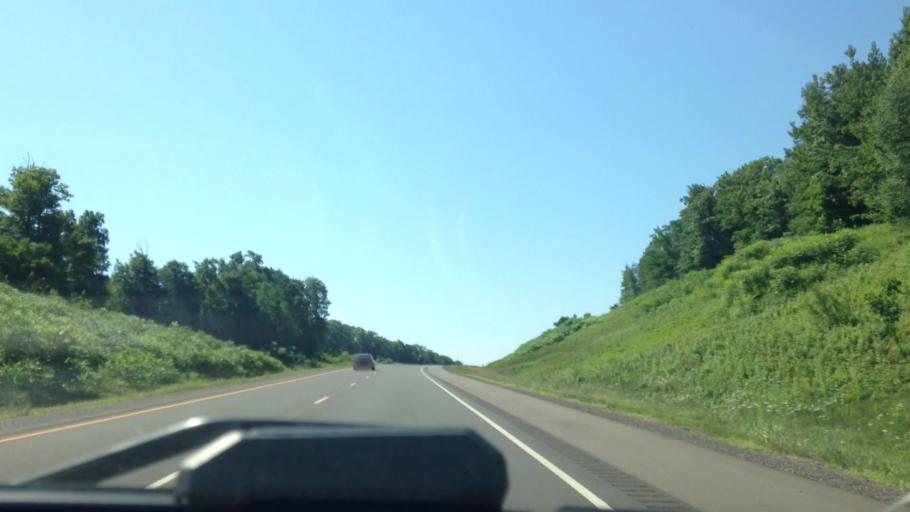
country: US
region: Wisconsin
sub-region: Washburn County
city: Spooner
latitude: 46.0074
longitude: -91.8351
